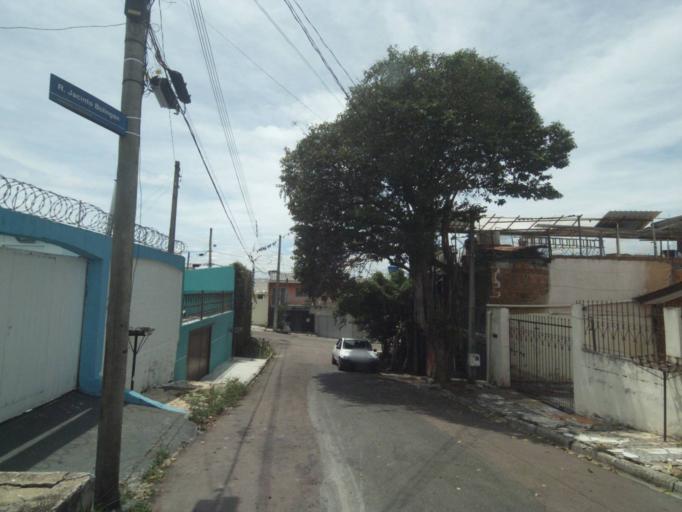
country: BR
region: Parana
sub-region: Curitiba
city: Curitiba
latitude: -25.4963
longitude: -49.3403
